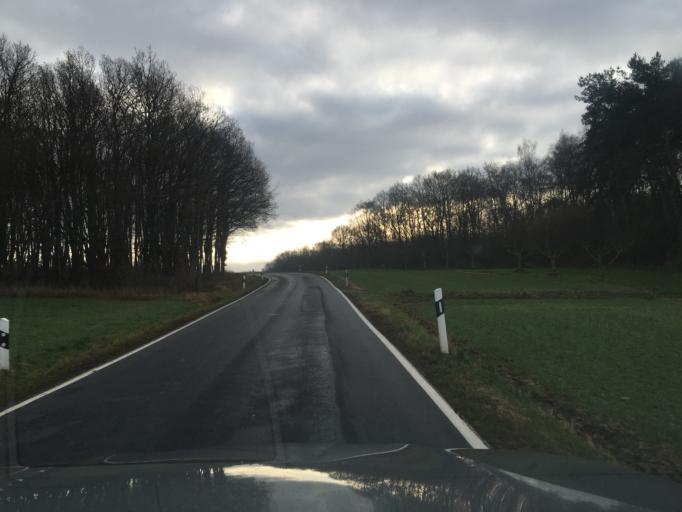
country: DE
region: Rheinland-Pfalz
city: Unkel
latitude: 50.5882
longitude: 7.1578
